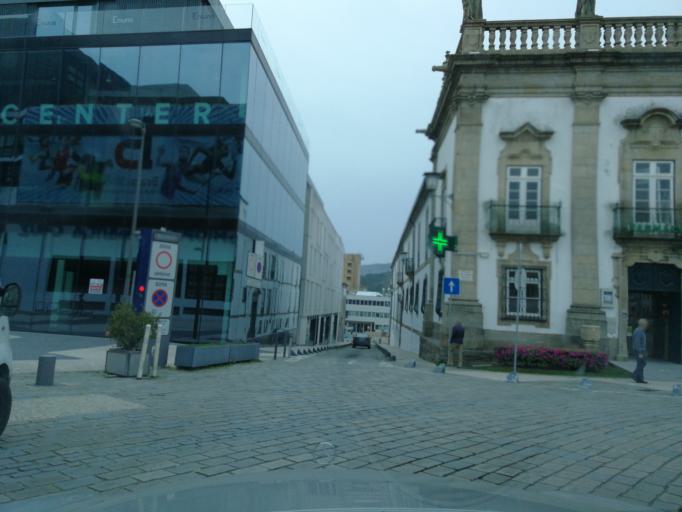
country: PT
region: Braga
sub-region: Braga
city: Braga
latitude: 41.5493
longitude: -8.4233
